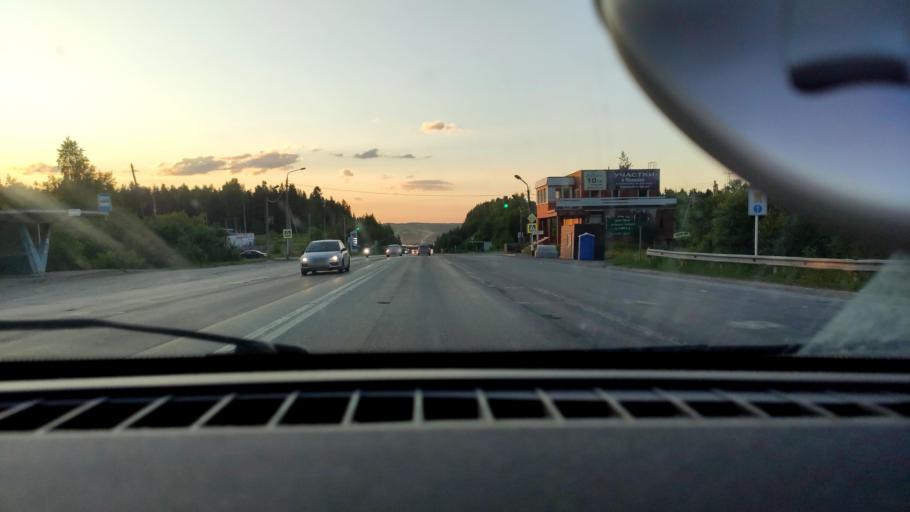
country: RU
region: Perm
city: Polazna
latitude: 58.1481
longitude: 56.4191
